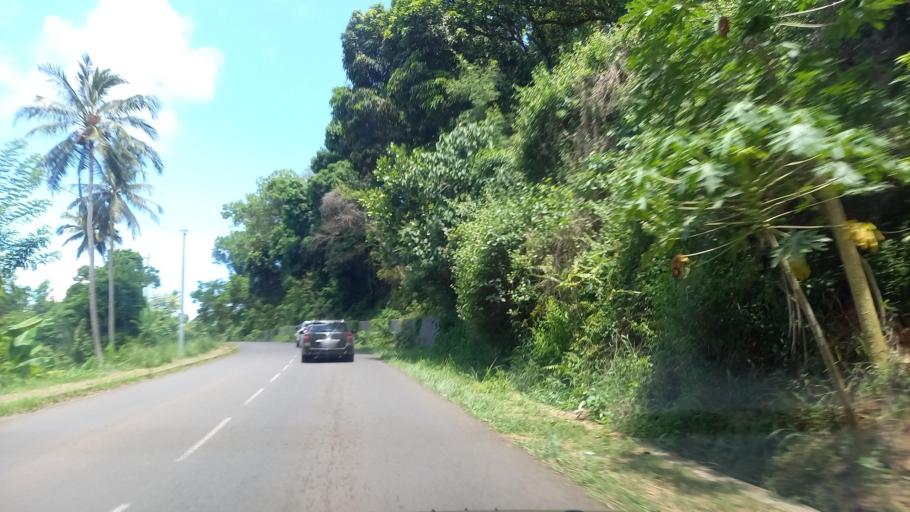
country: YT
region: Sada
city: Sada
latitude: -12.8530
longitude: 45.1056
